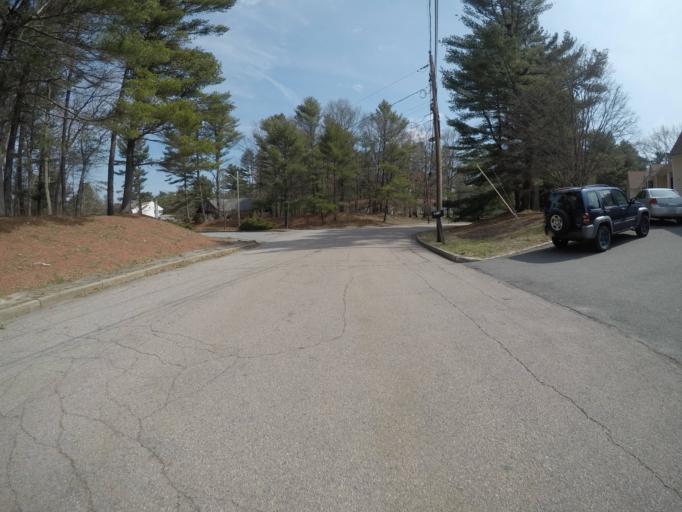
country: US
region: Massachusetts
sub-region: Bristol County
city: Easton
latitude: 42.0480
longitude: -71.1231
